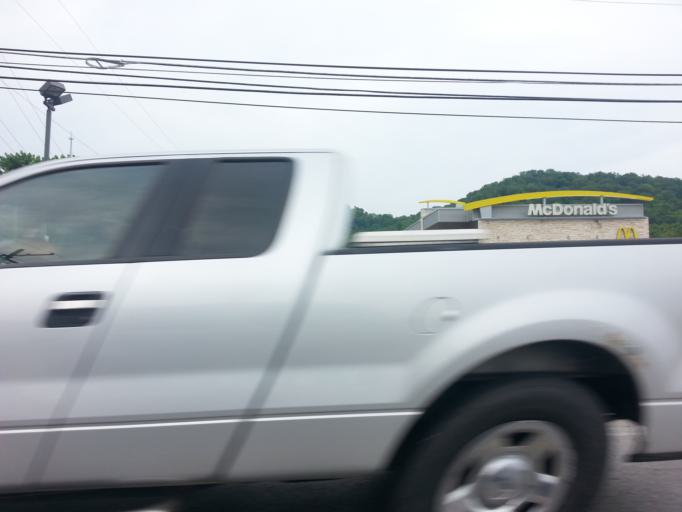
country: US
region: Ohio
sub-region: Brown County
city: Ripley
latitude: 38.7320
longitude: -83.8371
